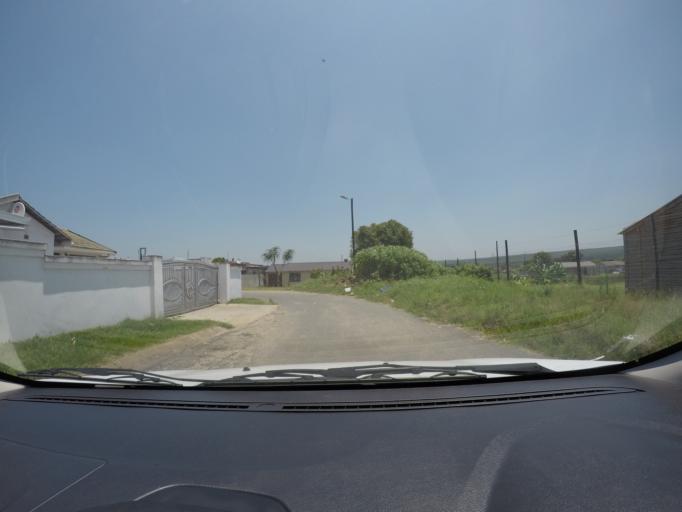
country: ZA
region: KwaZulu-Natal
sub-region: uThungulu District Municipality
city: eSikhawini
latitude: -28.8821
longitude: 31.9010
